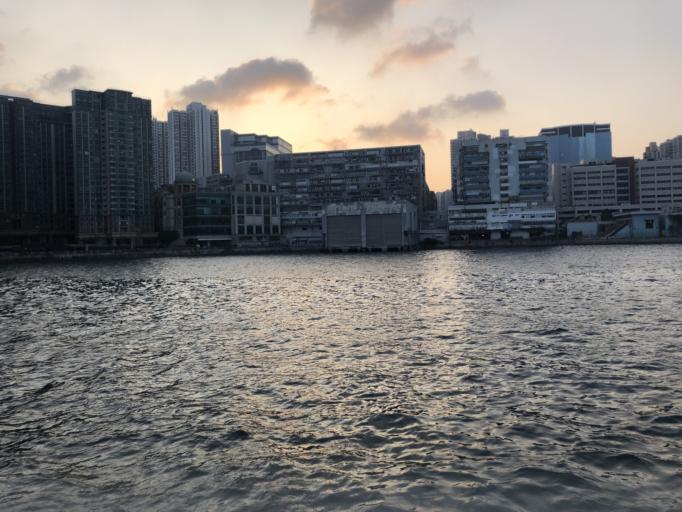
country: HK
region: Kowloon City
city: Kowloon
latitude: 22.3107
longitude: 114.1944
